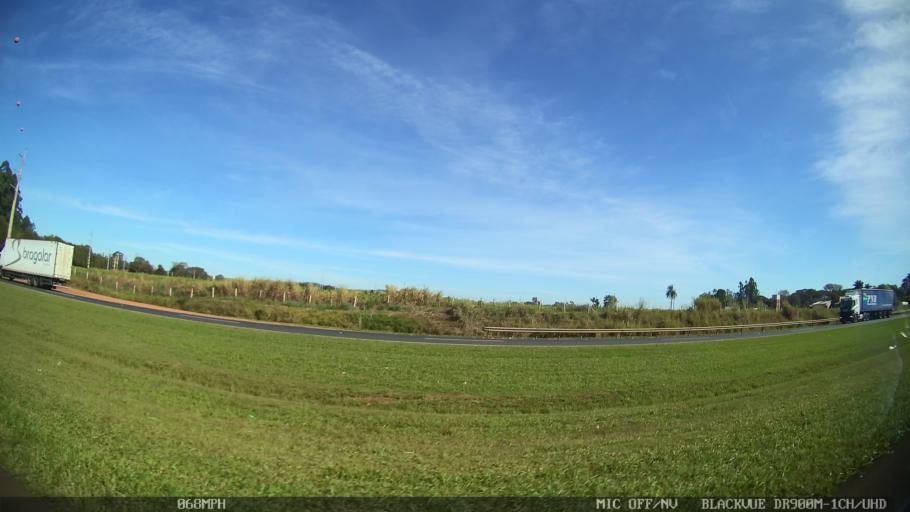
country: BR
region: Sao Paulo
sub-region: Leme
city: Leme
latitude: -22.2271
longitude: -47.3914
